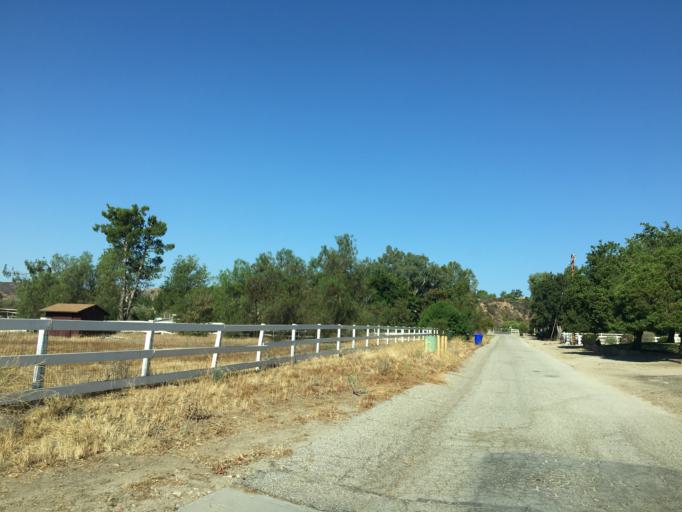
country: US
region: California
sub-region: Los Angeles County
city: Val Verde
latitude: 34.4709
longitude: -118.6606
